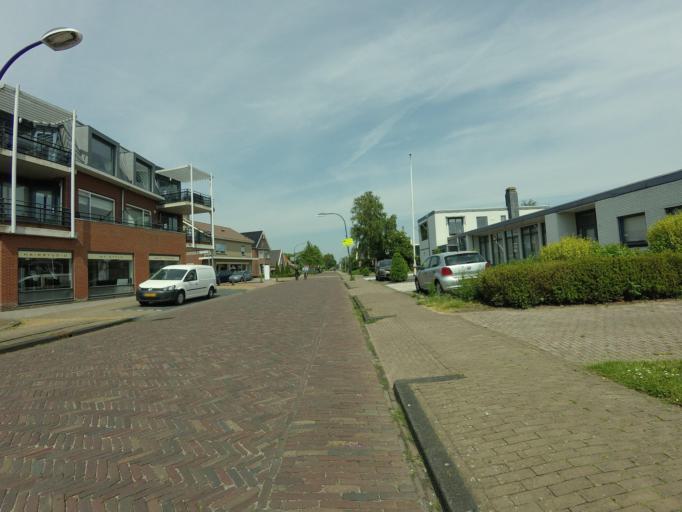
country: NL
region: North Holland
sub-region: Gemeente Hoorn
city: Hoorn
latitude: 52.6831
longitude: 5.0230
